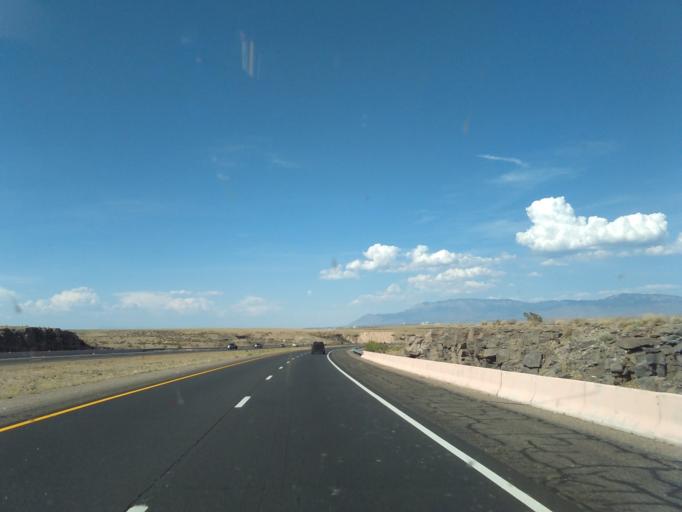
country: US
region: New Mexico
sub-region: Valencia County
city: Bosque Farms
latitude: 34.9306
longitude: -106.7164
